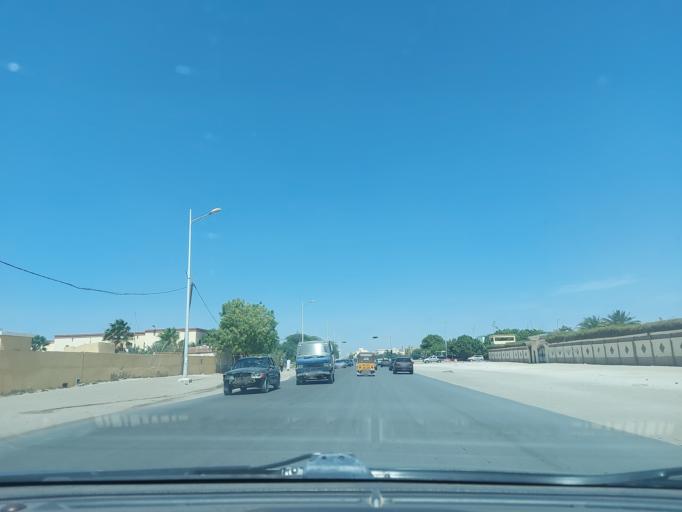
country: MR
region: Nouakchott
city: Nouakchott
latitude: 18.0798
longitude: -15.9676
